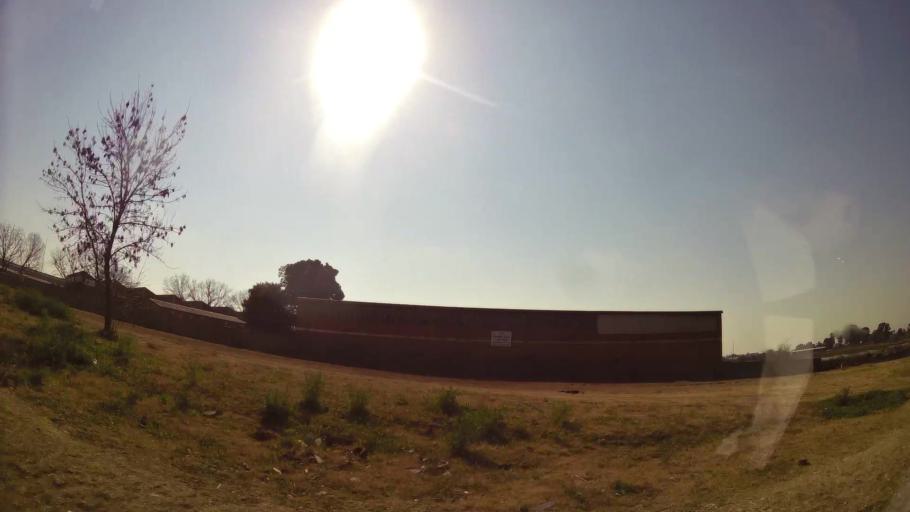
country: ZA
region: Gauteng
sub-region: Ekurhuleni Metropolitan Municipality
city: Benoni
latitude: -26.2080
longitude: 28.3110
